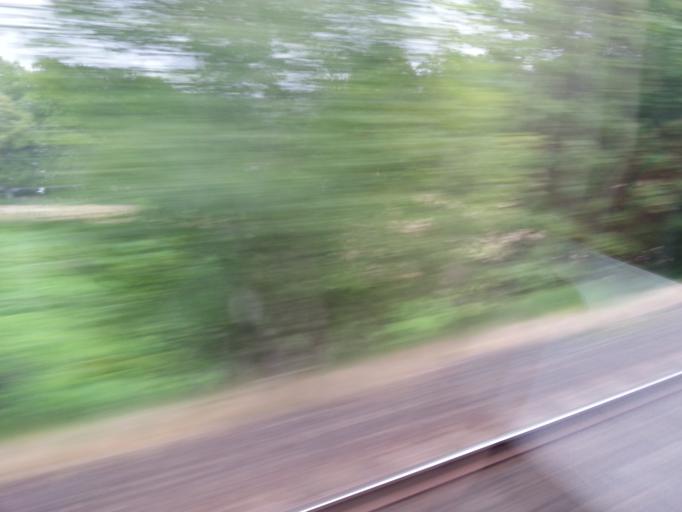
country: GB
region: Scotland
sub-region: Perth and Kinross
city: Luncarty
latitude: 56.4338
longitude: -3.4723
